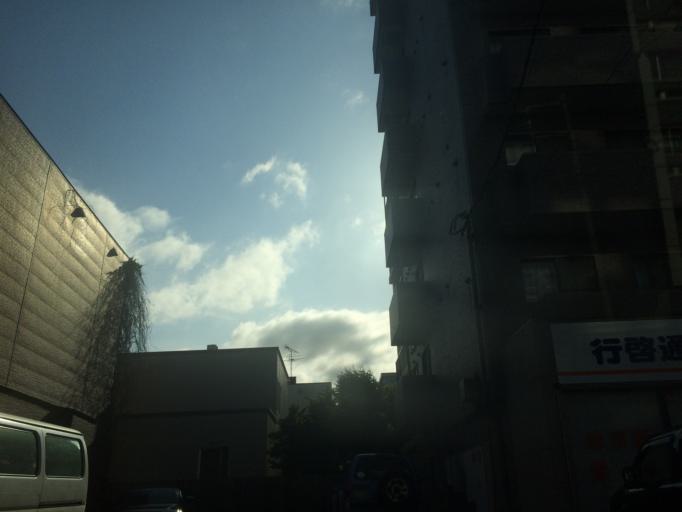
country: JP
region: Hokkaido
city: Sapporo
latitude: 43.0409
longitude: 141.3507
